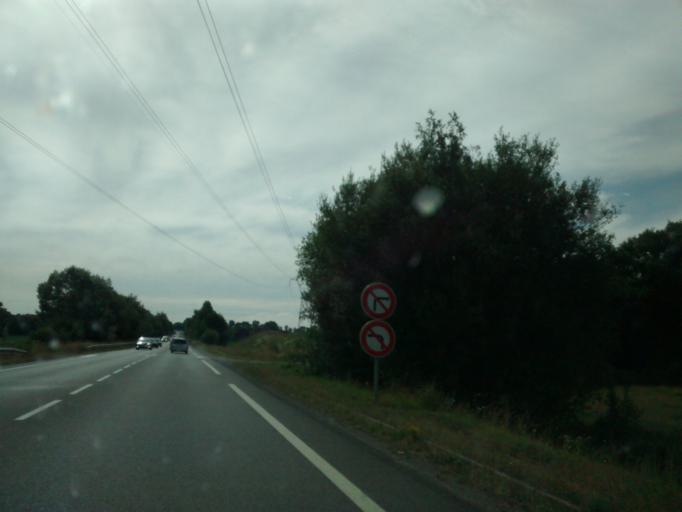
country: FR
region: Brittany
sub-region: Departement d'Ille-et-Vilaine
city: Betton
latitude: 48.1624
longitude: -1.6604
